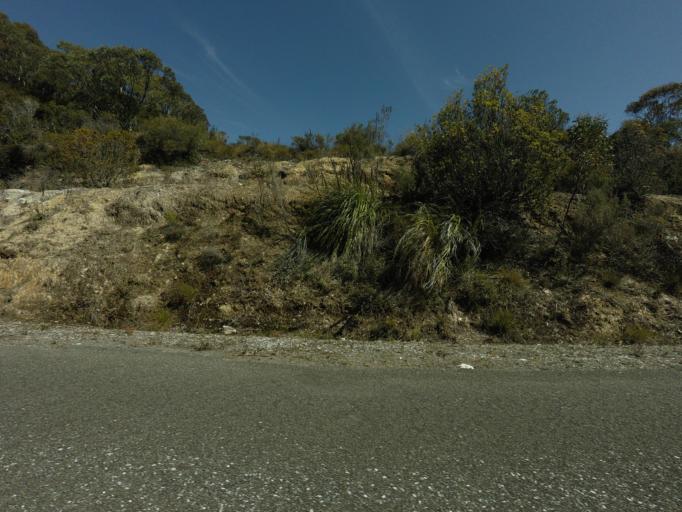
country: AU
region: Tasmania
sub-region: Huon Valley
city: Geeveston
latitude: -42.8362
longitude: 146.1414
